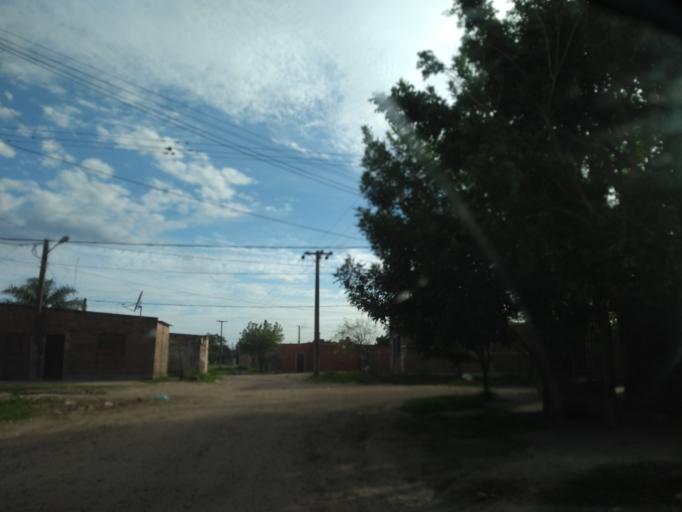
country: AR
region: Chaco
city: Resistencia
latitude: -27.4530
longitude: -58.9657
